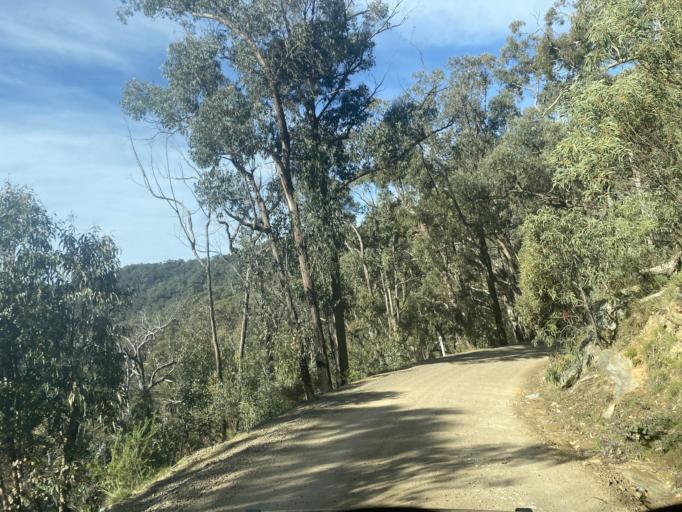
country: AU
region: Victoria
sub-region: Mansfield
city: Mansfield
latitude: -36.8380
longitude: 146.1652
